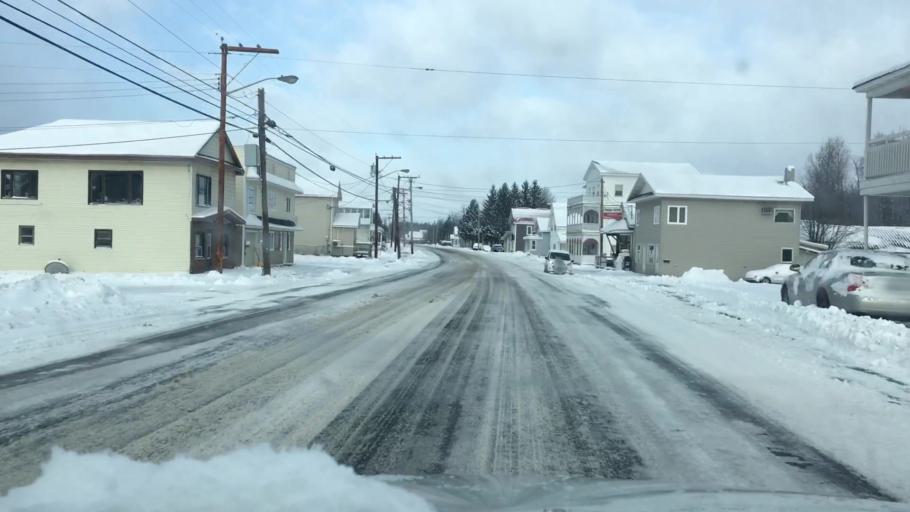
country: US
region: Maine
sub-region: Aroostook County
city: Van Buren
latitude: 47.1859
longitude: -67.9563
